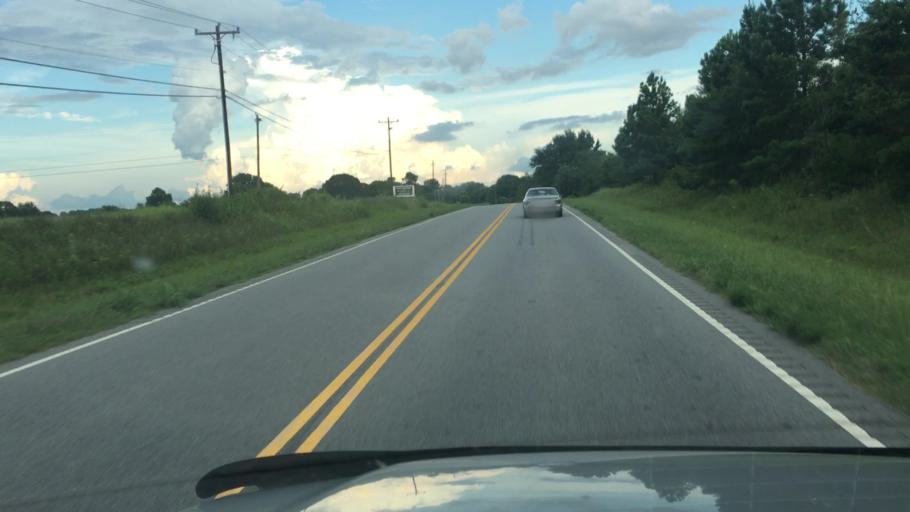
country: US
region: South Carolina
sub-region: Spartanburg County
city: Mayo
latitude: 35.1333
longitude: -81.8006
